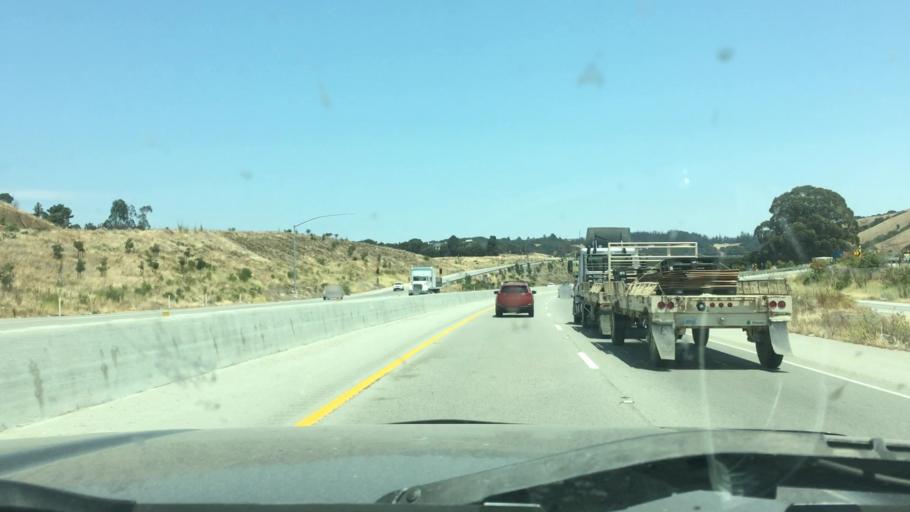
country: US
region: California
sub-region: San Benito County
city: Aromas
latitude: 36.8561
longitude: -121.6297
